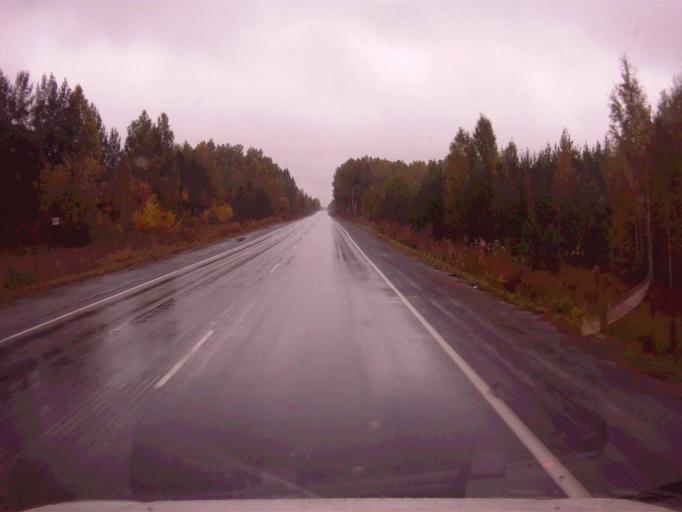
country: RU
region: Chelyabinsk
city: Tayginka
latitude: 55.5340
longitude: 60.6467
